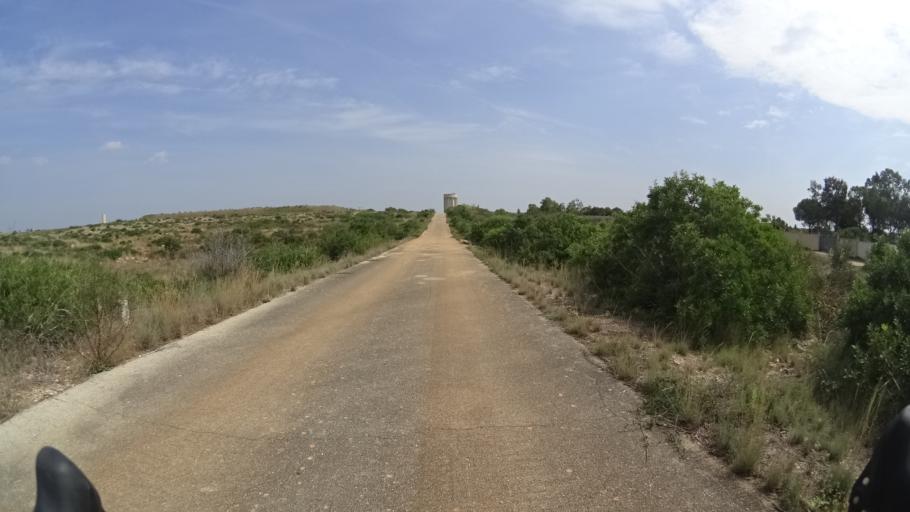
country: IT
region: Apulia
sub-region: Provincia di Brindisi
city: San Pancrazio Salentino
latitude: 40.3465
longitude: 17.8241
